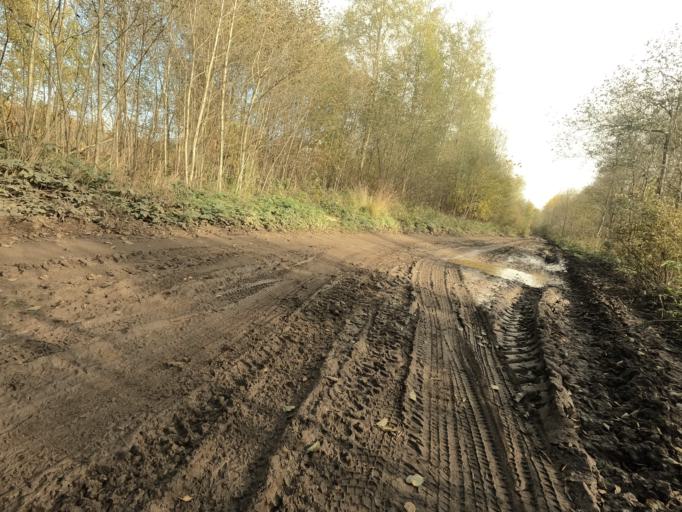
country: RU
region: Novgorod
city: Batetskiy
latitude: 58.8791
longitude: 30.7459
